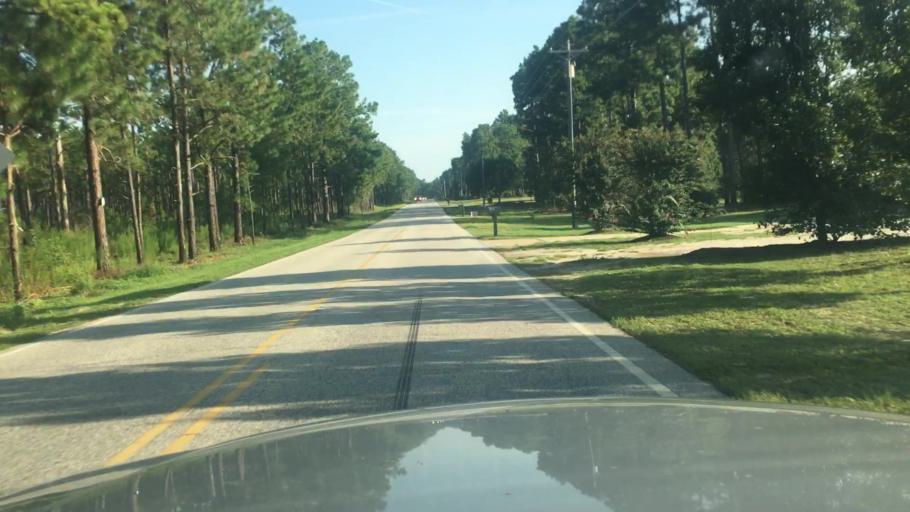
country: US
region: North Carolina
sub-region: Harnett County
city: Walkertown
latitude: 35.2162
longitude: -78.8650
